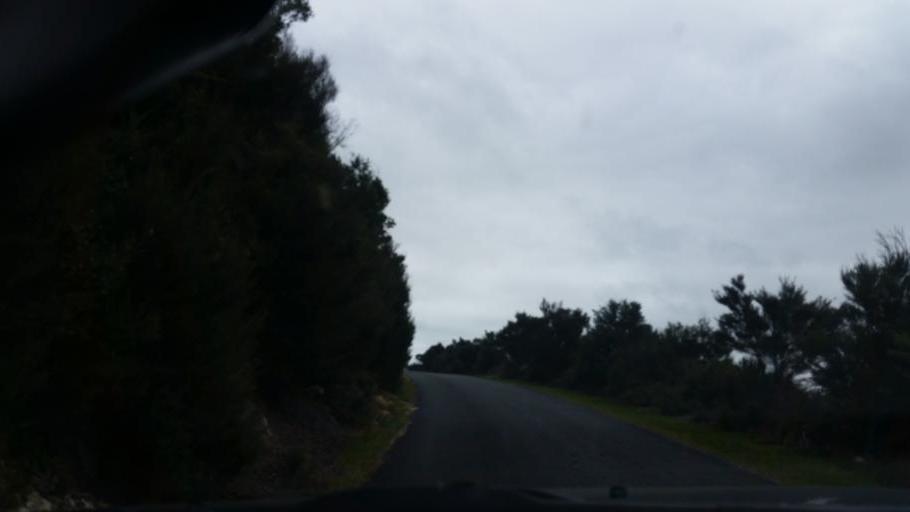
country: NZ
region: Northland
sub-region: Kaipara District
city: Dargaville
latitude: -35.8123
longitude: 173.6549
